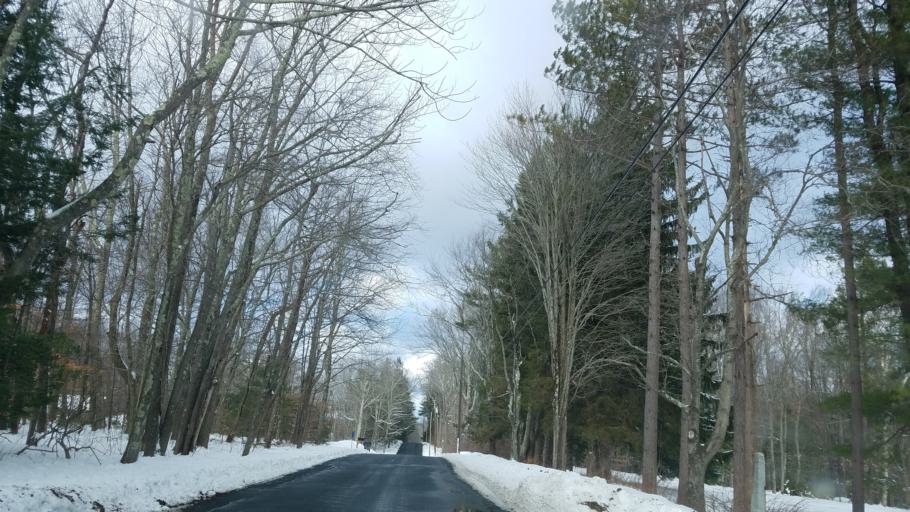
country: US
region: Connecticut
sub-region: Litchfield County
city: Winsted
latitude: 41.9717
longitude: -73.0771
